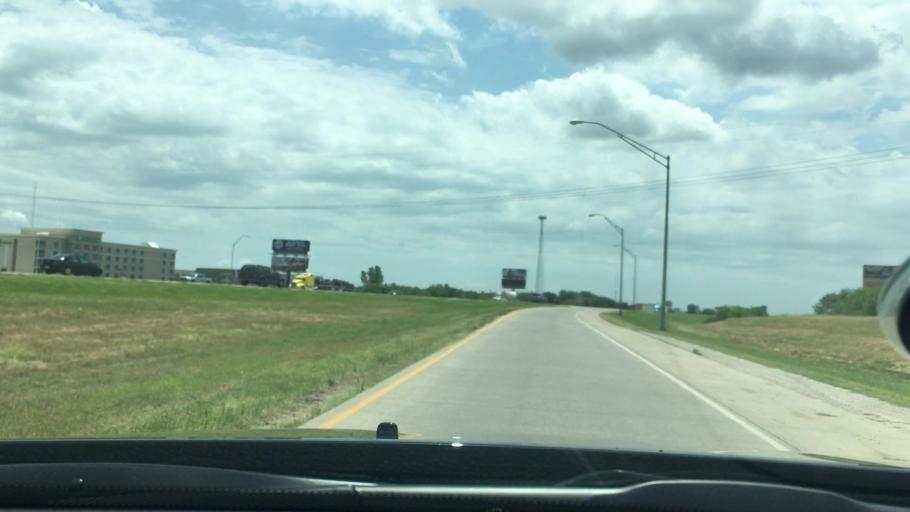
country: US
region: Oklahoma
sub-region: Carter County
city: Ardmore
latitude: 34.2003
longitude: -97.1647
